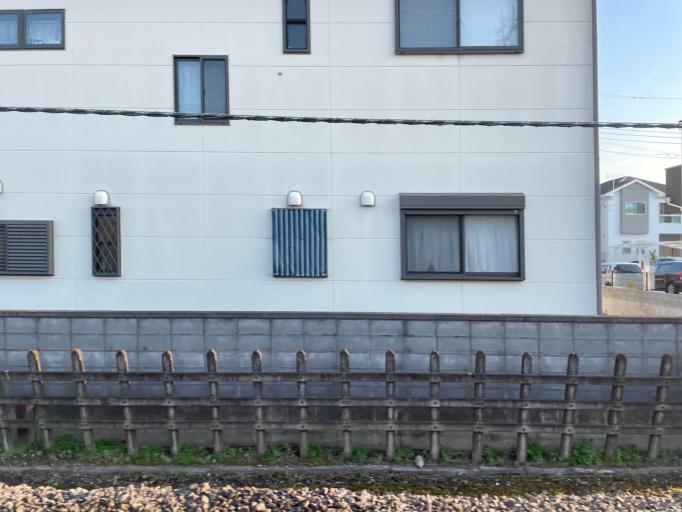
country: JP
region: Gunma
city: Takasaki
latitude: 36.3400
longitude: 138.9913
